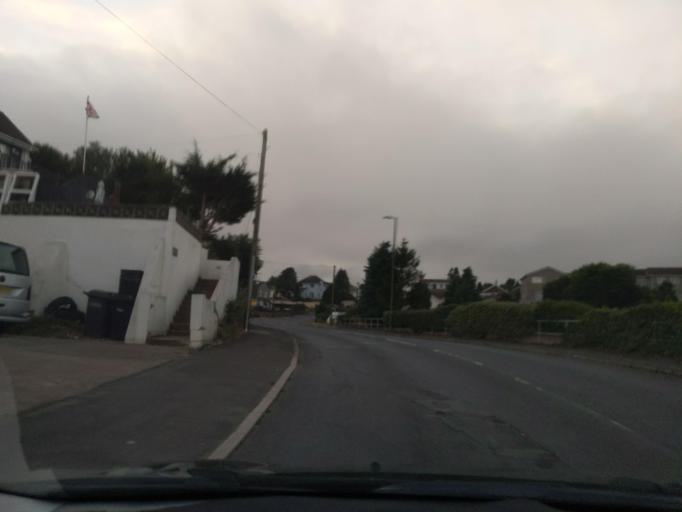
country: GB
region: England
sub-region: Devon
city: Marldon
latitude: 50.4482
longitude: -3.5848
